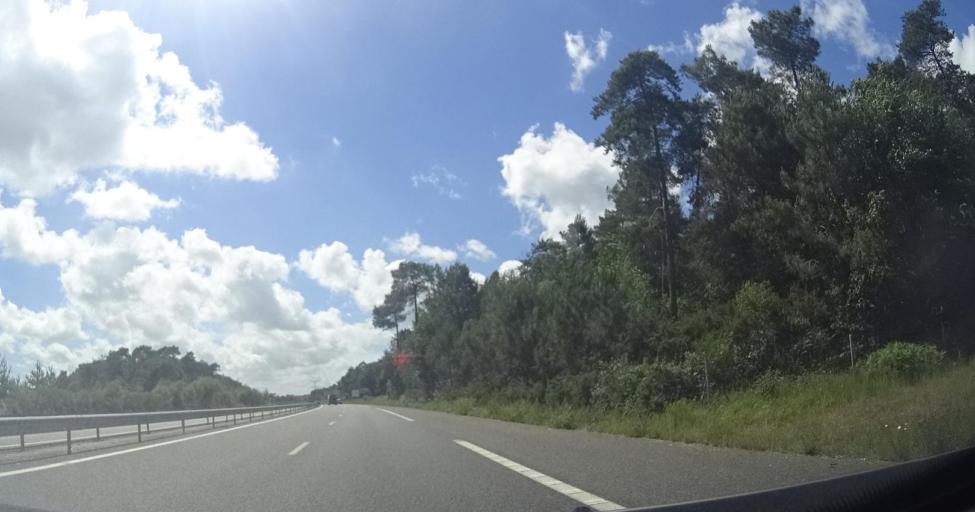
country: FR
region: Brittany
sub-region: Departement du Morbihan
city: Pluherlin
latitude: 47.6697
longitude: -2.3406
